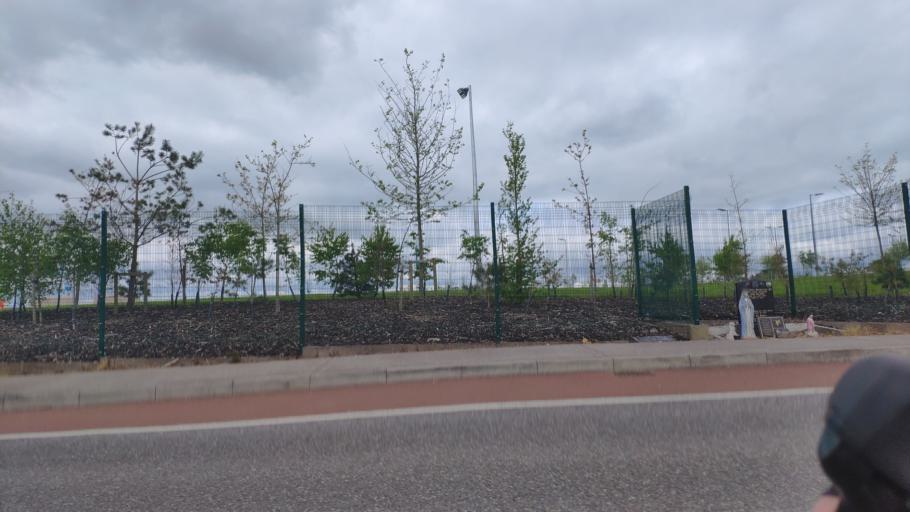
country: IE
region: Munster
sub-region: County Cork
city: Cork
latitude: 51.9051
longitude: -8.5163
